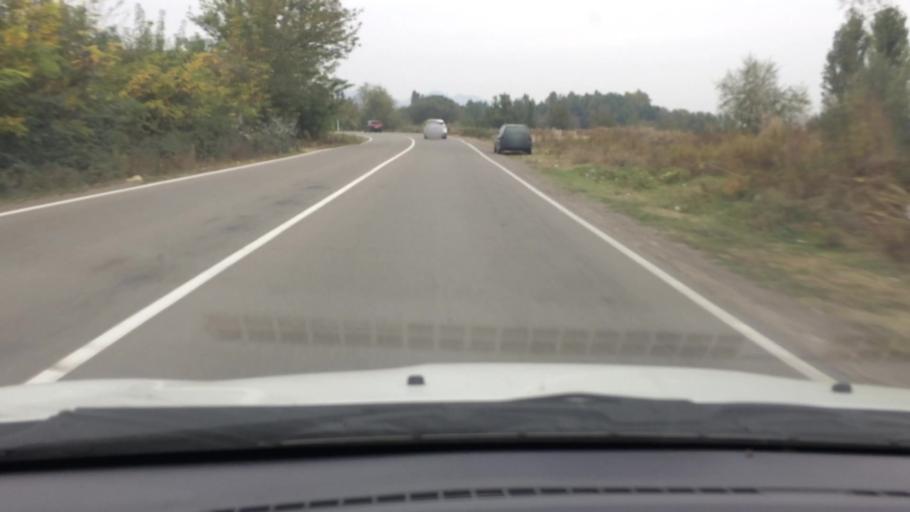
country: AM
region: Tavush
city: Bagratashen
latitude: 41.2569
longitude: 44.7977
